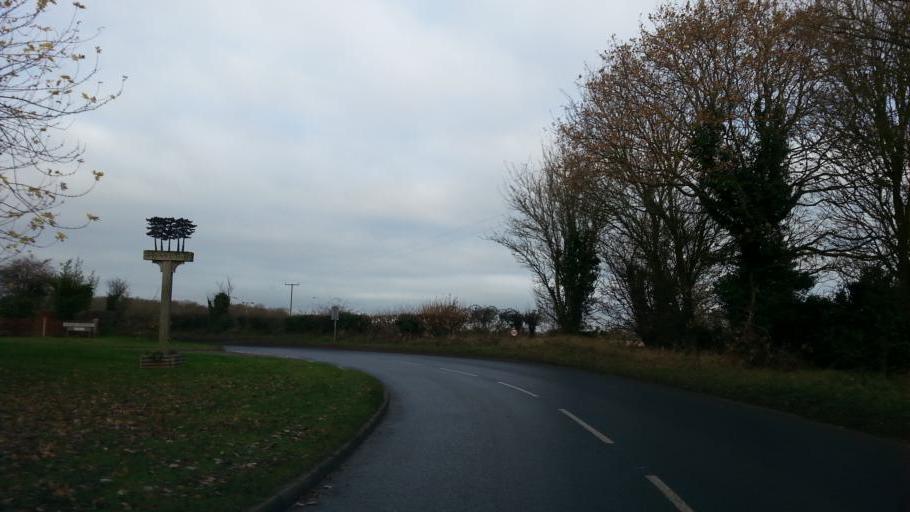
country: GB
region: England
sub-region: Suffolk
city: Wickham Market
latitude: 52.1445
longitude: 1.4438
